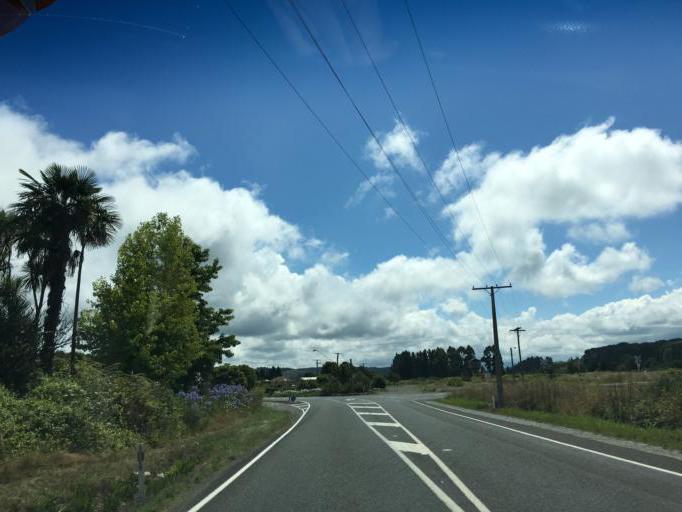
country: NZ
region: Hawke's Bay
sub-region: Wairoa District
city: Wairoa
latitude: -39.0747
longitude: 177.1472
